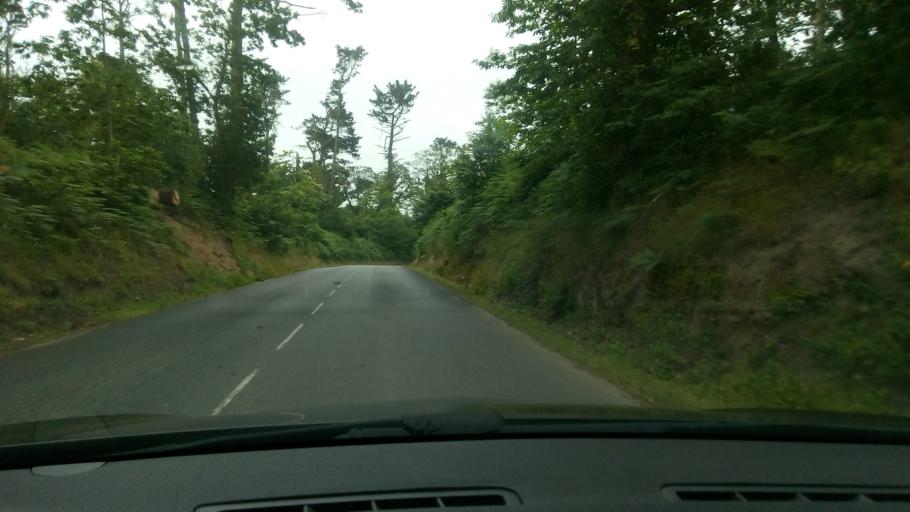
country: FR
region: Brittany
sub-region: Departement du Finistere
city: Le Conquet
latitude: 48.3721
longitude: -4.7463
